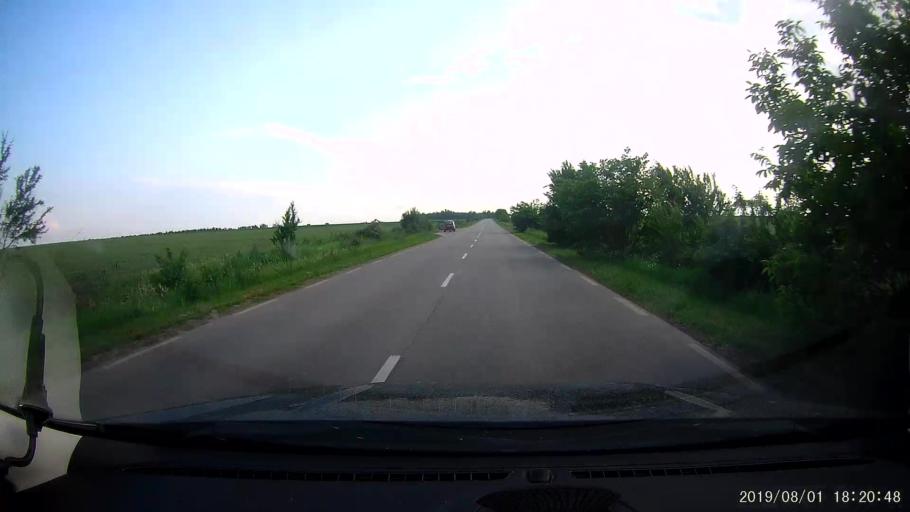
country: BG
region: Shumen
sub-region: Obshtina Kaolinovo
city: Kaolinovo
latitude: 43.6638
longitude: 27.0831
